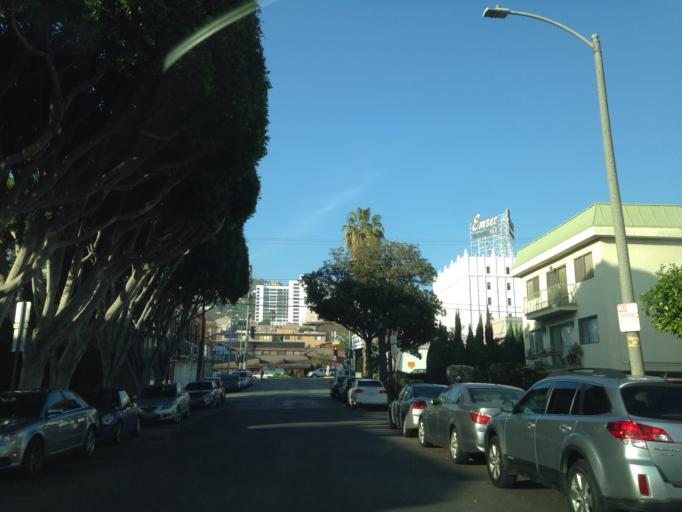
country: US
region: California
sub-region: Los Angeles County
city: West Hollywood
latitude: 34.0896
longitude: -118.3743
